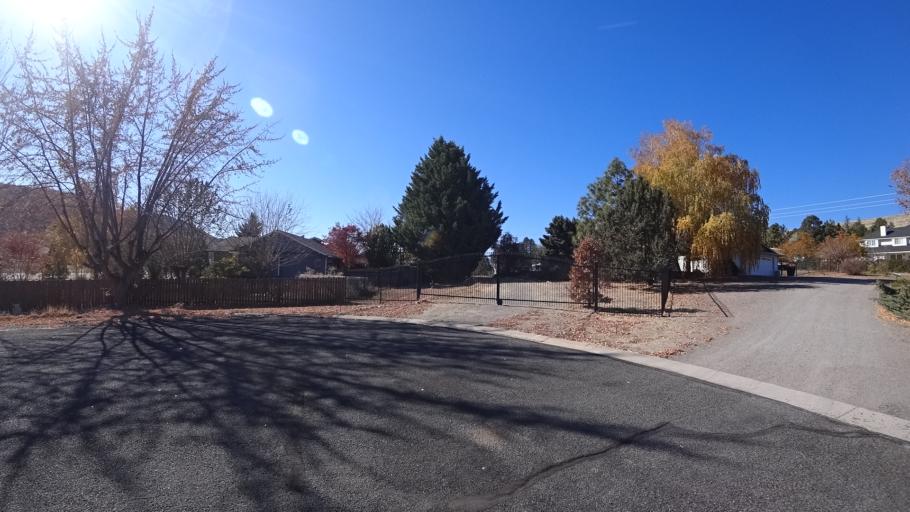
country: US
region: California
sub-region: Siskiyou County
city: Yreka
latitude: 41.7410
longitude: -122.6120
